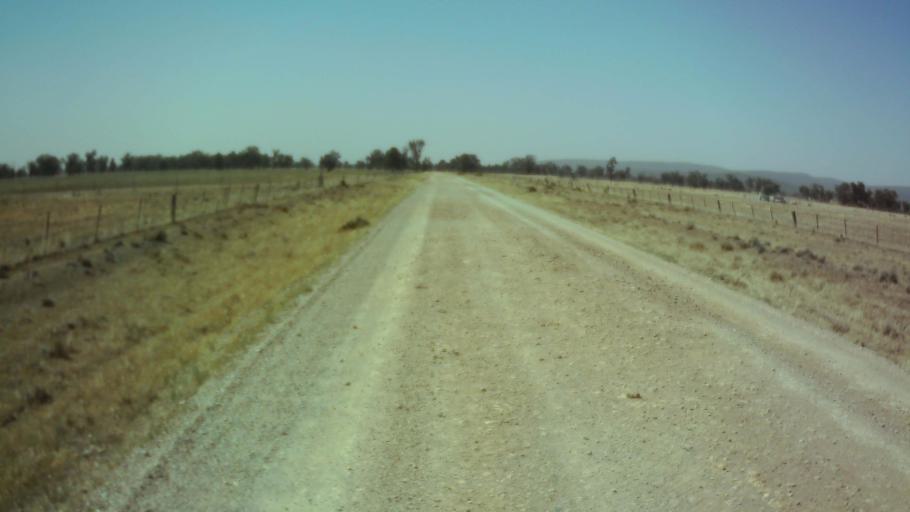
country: AU
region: New South Wales
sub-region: Weddin
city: Grenfell
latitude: -34.0297
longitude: 147.9127
